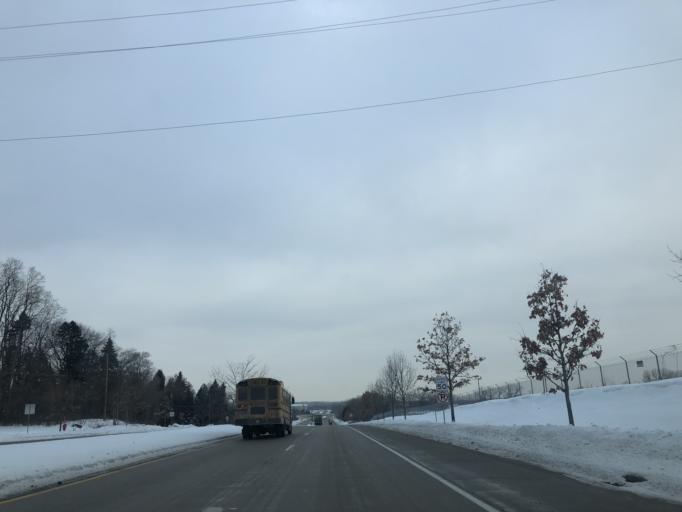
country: US
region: Minnesota
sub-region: Ramsey County
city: Shoreview
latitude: 45.0794
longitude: -93.1638
